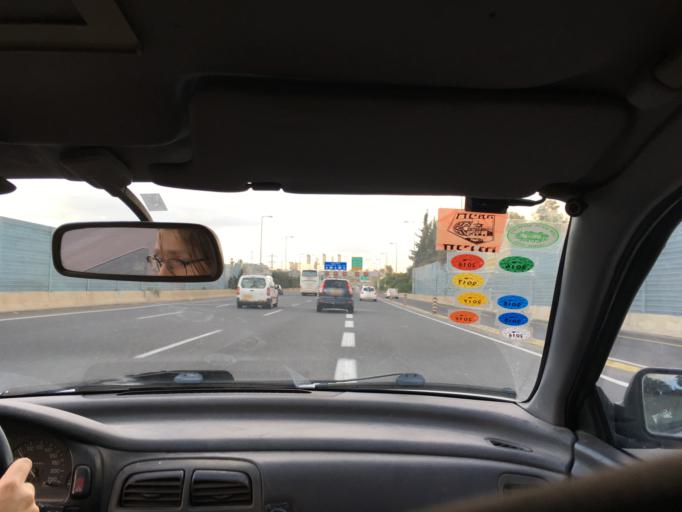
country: IL
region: Tel Aviv
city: Ramat Gan
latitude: 32.0929
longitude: 34.8016
